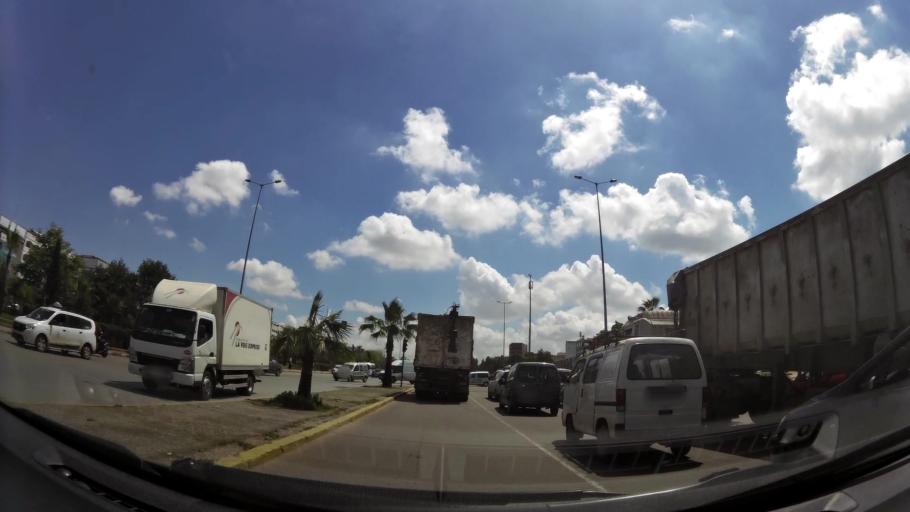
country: MA
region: Grand Casablanca
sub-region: Casablanca
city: Casablanca
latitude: 33.5416
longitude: -7.5799
